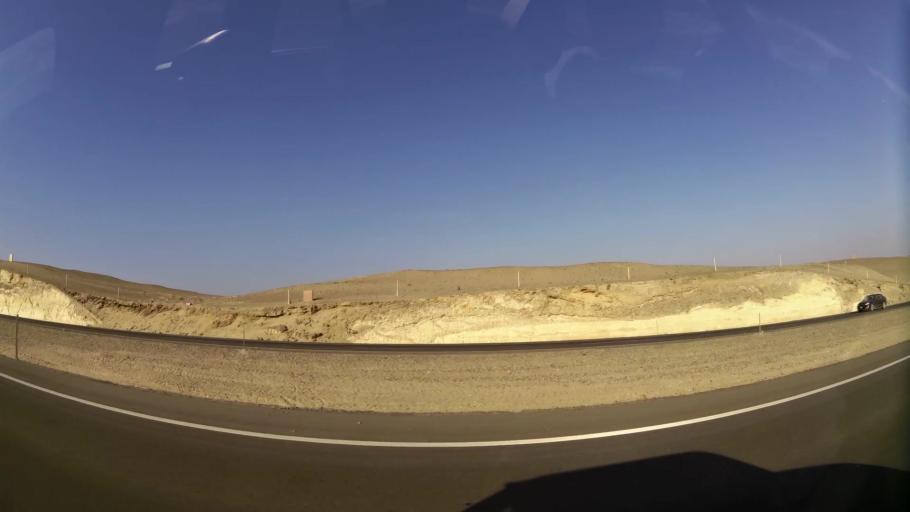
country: PE
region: Ica
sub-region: Provincia de Pisco
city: San Clemente
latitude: -13.6532
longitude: -76.1738
